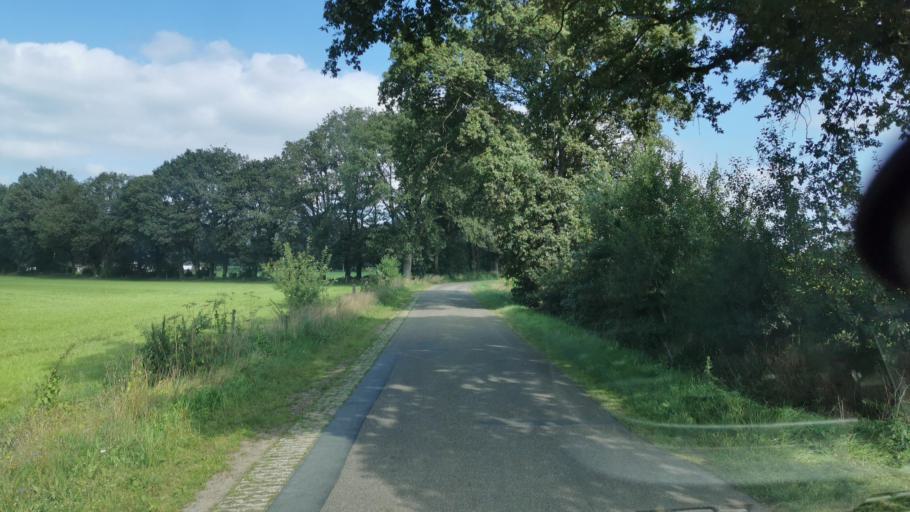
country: NL
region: Overijssel
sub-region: Gemeente Oldenzaal
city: Oldenzaal
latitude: 52.3429
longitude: 6.8476
